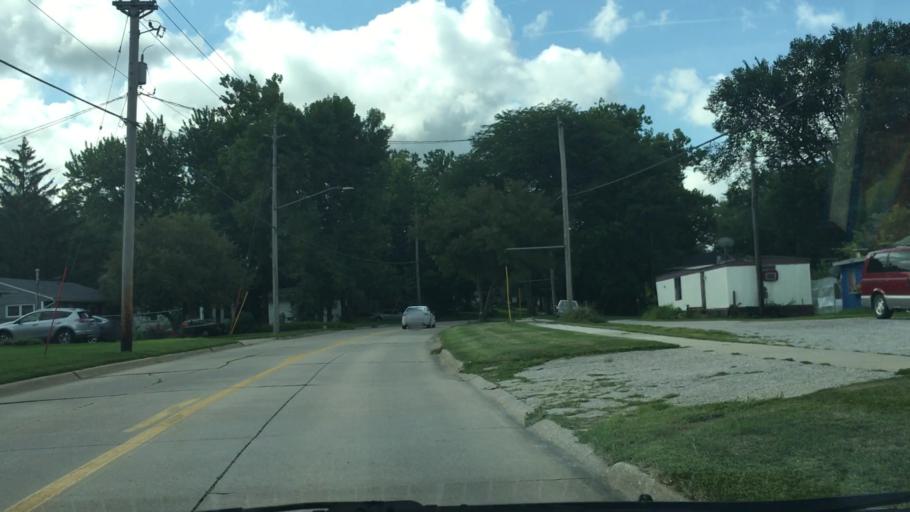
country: US
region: Iowa
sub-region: Johnson County
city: Iowa City
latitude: 41.6827
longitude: -91.5216
